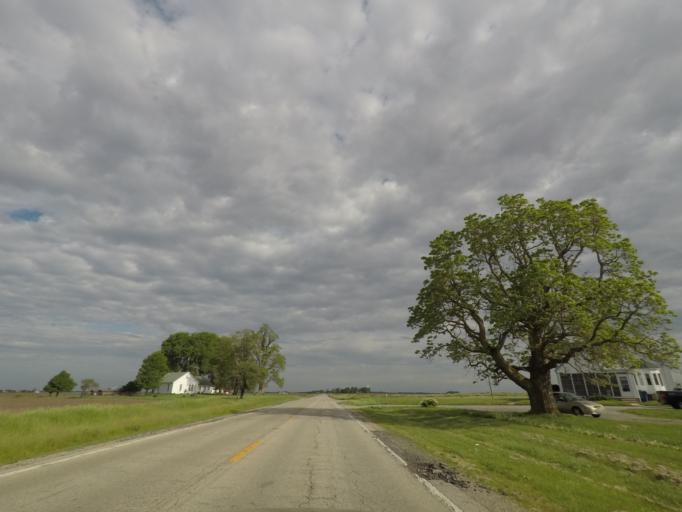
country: US
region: Illinois
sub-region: Logan County
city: Mount Pulaski
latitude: 40.0766
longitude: -89.2971
